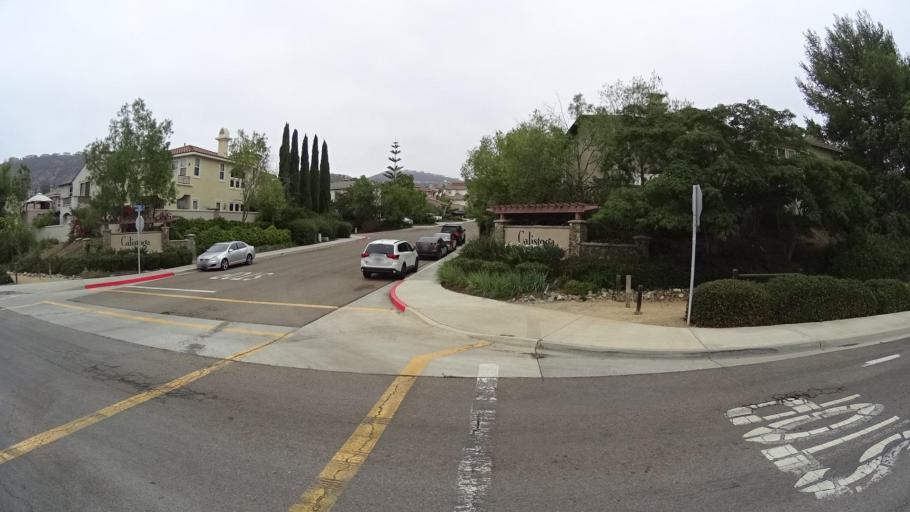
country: US
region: California
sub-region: San Diego County
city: Lake San Marcos
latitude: 33.0965
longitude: -117.1965
